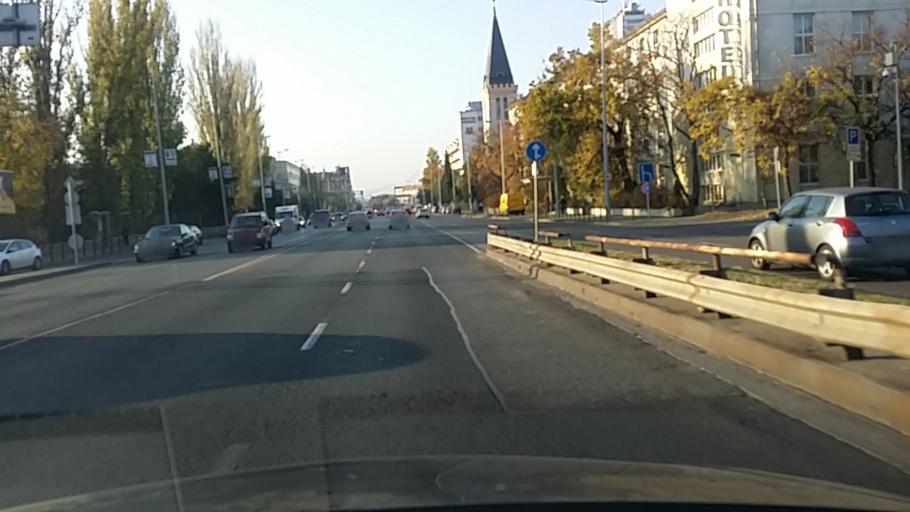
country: HU
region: Budapest
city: Budapest VIII. keruelet
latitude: 47.4768
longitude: 19.0954
